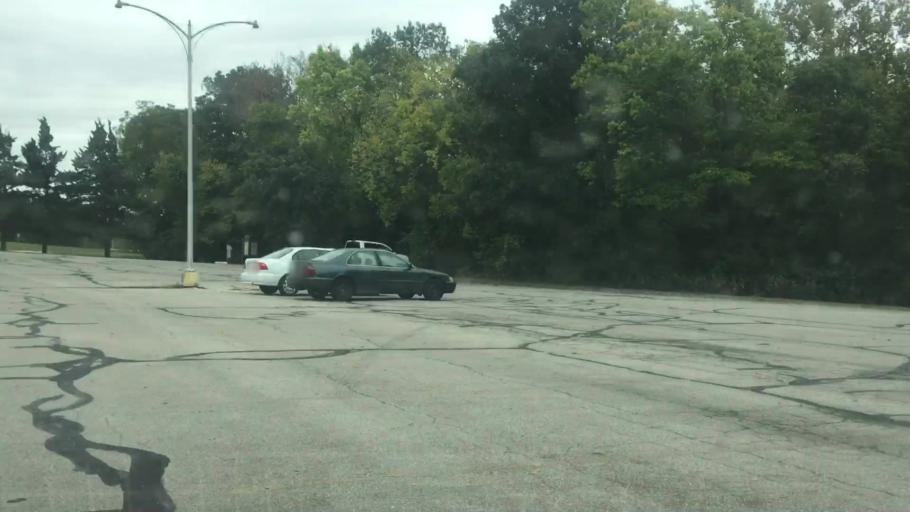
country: US
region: Kansas
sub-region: Johnson County
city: Lenexa
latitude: 38.9822
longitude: -94.7880
